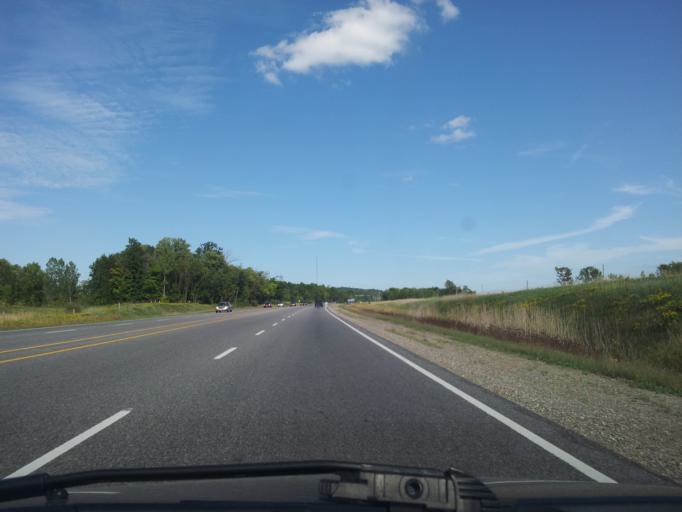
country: CA
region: Ontario
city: Kitchener
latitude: 43.3884
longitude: -80.6764
